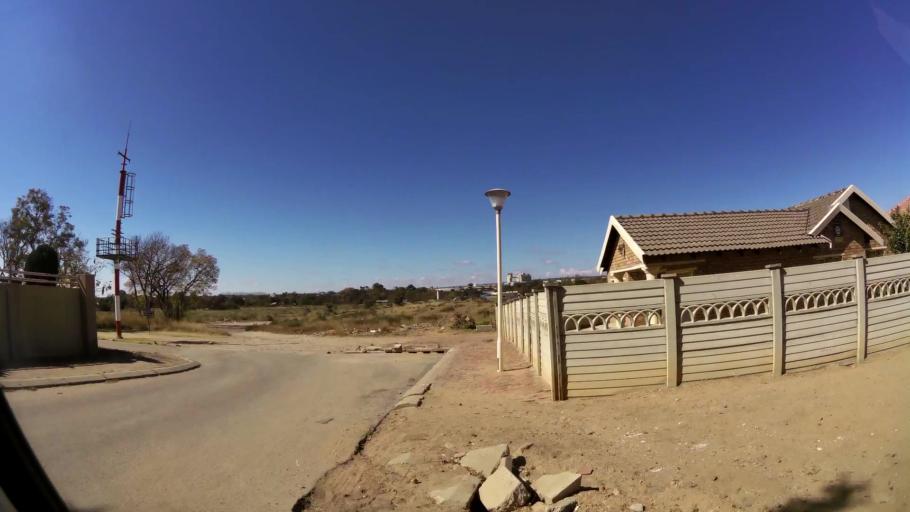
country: ZA
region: Limpopo
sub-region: Capricorn District Municipality
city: Polokwane
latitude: -23.8679
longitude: 29.4317
